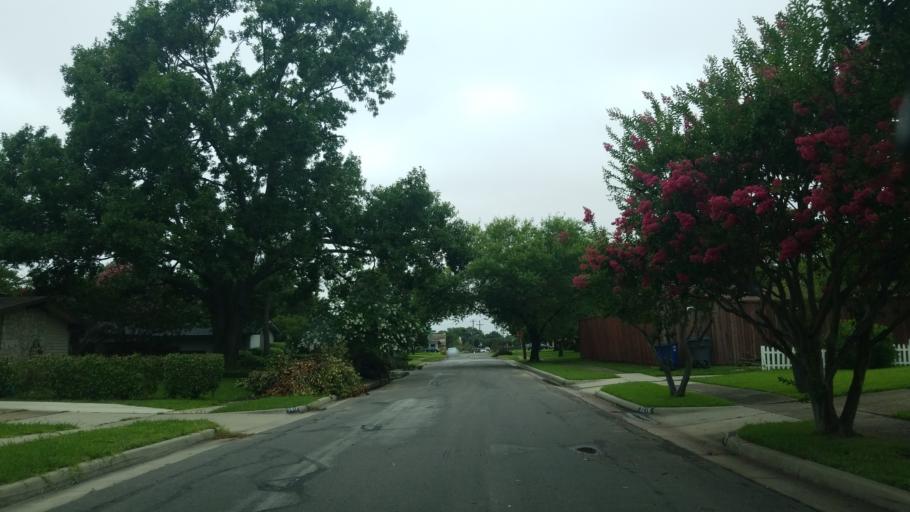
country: US
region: Texas
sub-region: Dallas County
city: Farmers Branch
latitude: 32.9067
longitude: -96.8697
